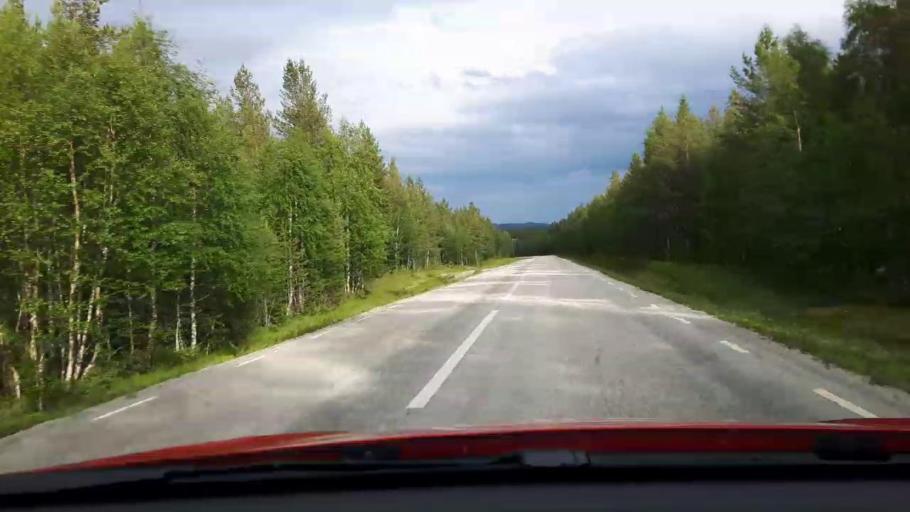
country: SE
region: Jaemtland
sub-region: Bergs Kommun
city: Hoverberg
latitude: 62.6665
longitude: 14.0396
